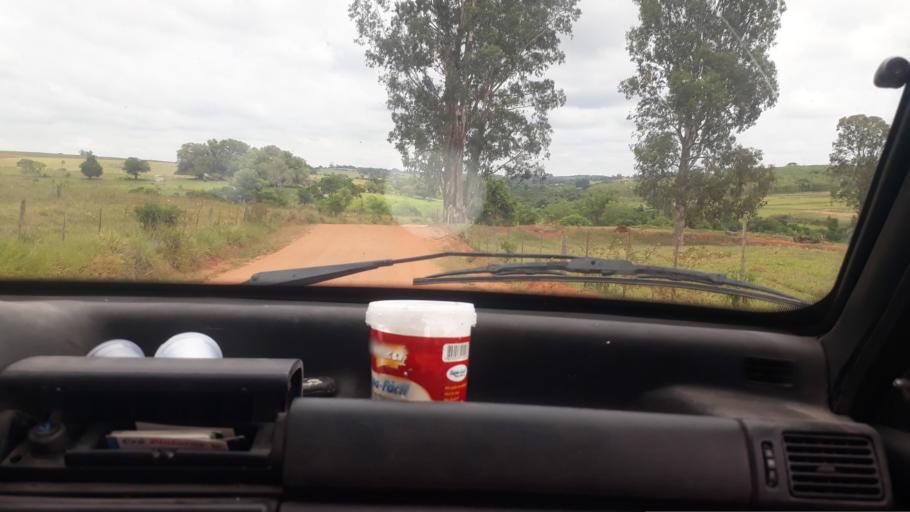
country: BR
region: Sao Paulo
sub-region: Regente Feijo
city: Regente Feijo
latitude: -22.2454
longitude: -51.2969
